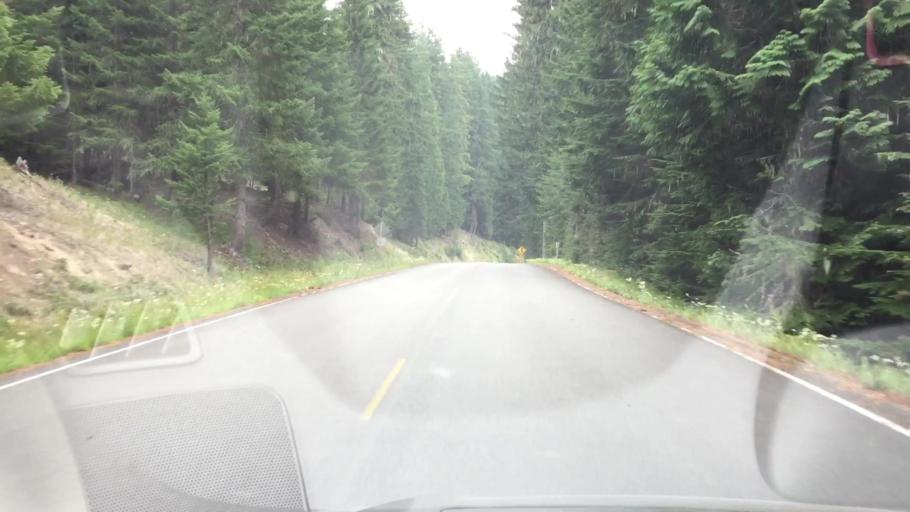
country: US
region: Washington
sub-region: Klickitat County
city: White Salmon
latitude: 46.2131
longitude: -121.6336
